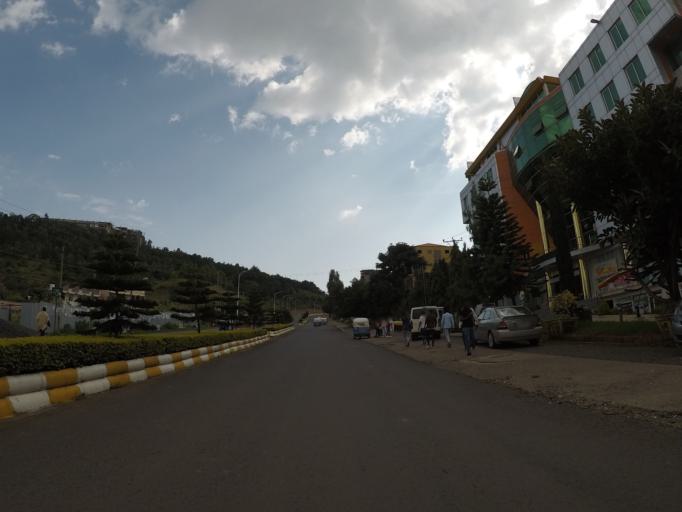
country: ET
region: Amhara
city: Gondar
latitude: 12.5931
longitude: 37.4466
